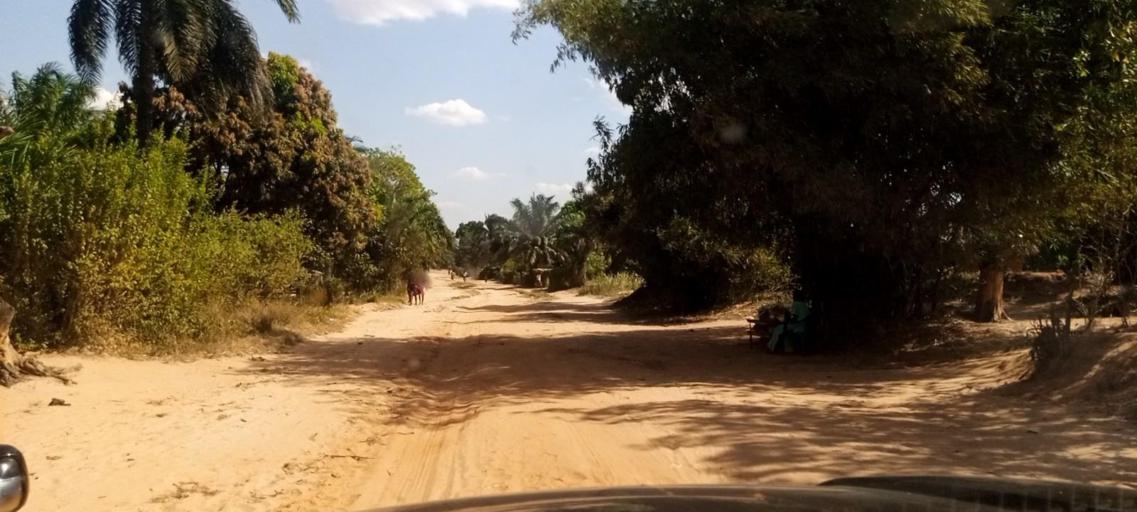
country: CD
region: Kasai-Oriental
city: Kabinda
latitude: -6.1316
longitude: 24.5140
